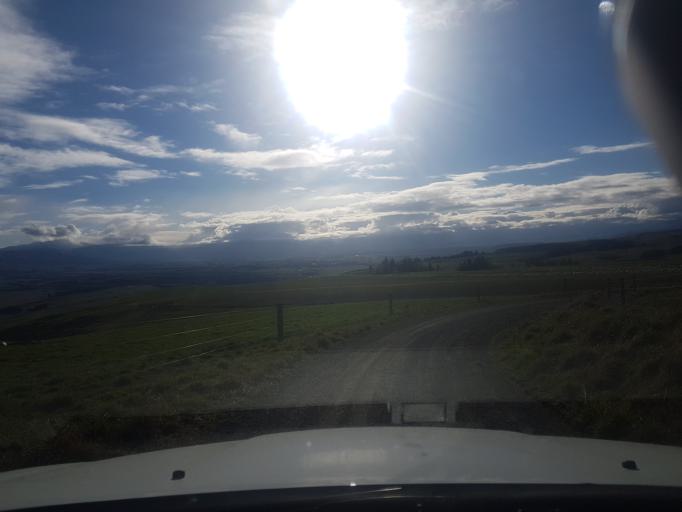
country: NZ
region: Canterbury
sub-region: Timaru District
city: Pleasant Point
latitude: -44.1733
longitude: 170.8886
